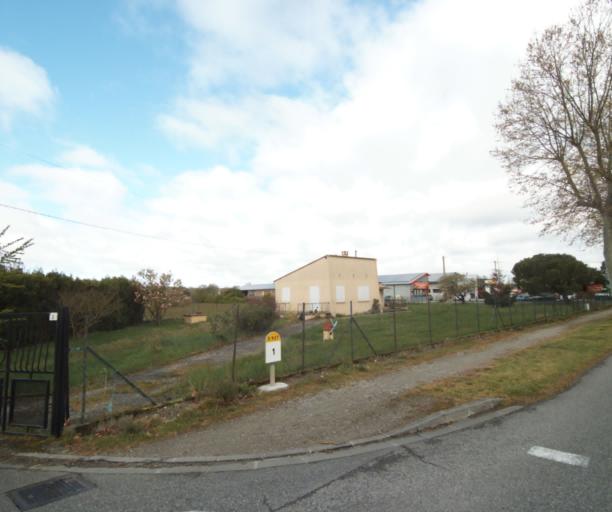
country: FR
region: Midi-Pyrenees
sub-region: Departement de l'Ariege
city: Saverdun
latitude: 43.2432
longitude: 1.5706
